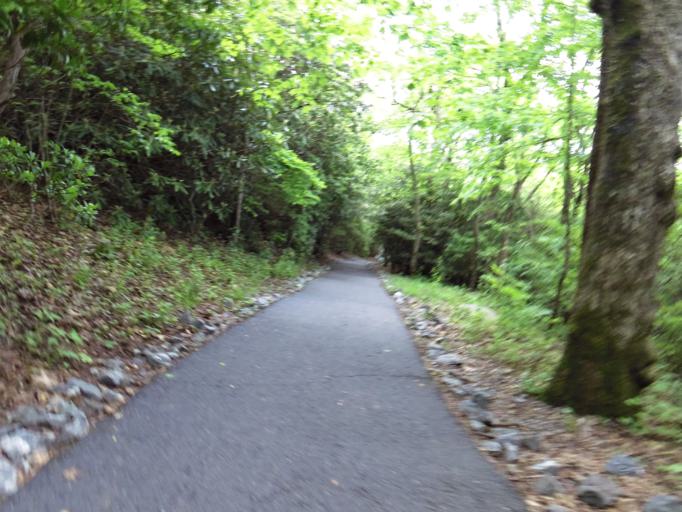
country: US
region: Georgia
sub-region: Towns County
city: Hiawassee
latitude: 34.8717
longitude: -83.8102
